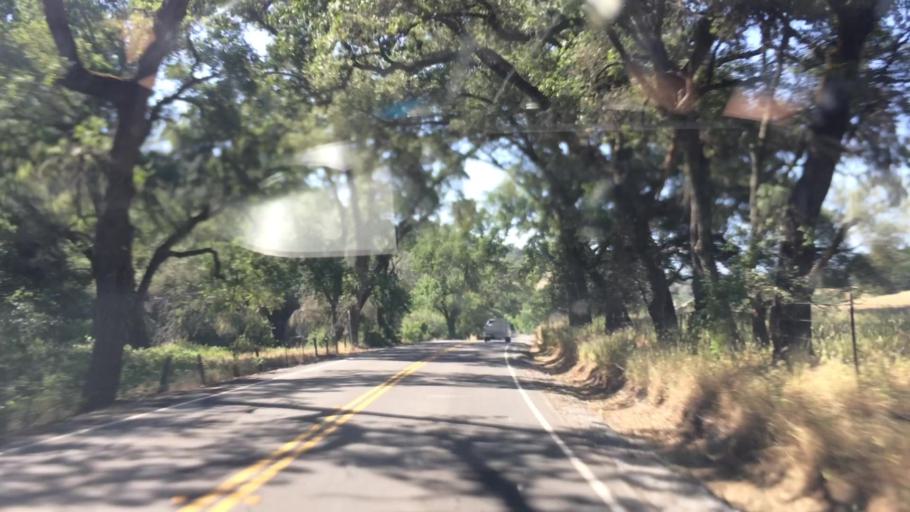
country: US
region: California
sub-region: Amador County
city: Plymouth
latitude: 38.5177
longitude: -120.9524
